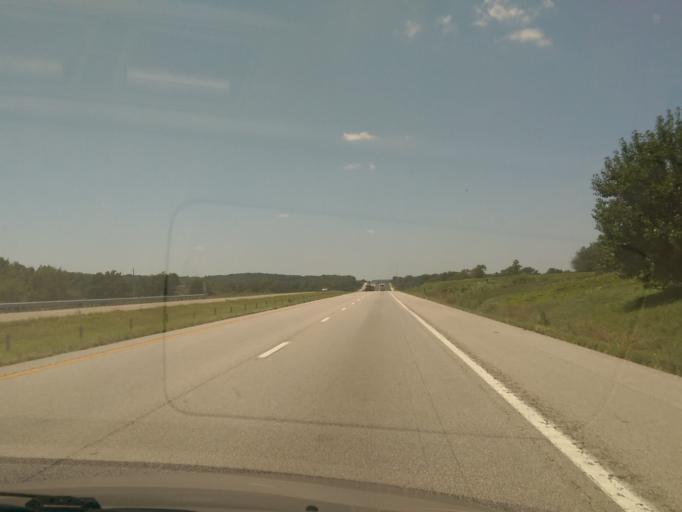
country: US
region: Missouri
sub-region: Cooper County
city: Boonville
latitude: 38.9353
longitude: -92.8657
